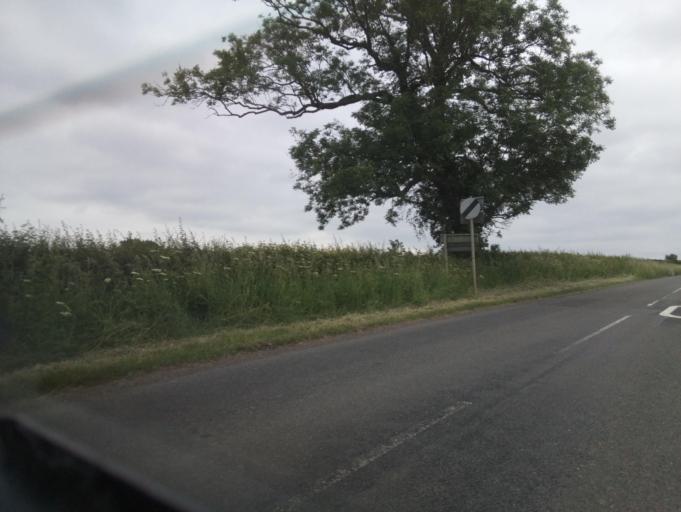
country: GB
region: England
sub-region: Leicestershire
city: Melton Mowbray
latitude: 52.7104
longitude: -0.8327
